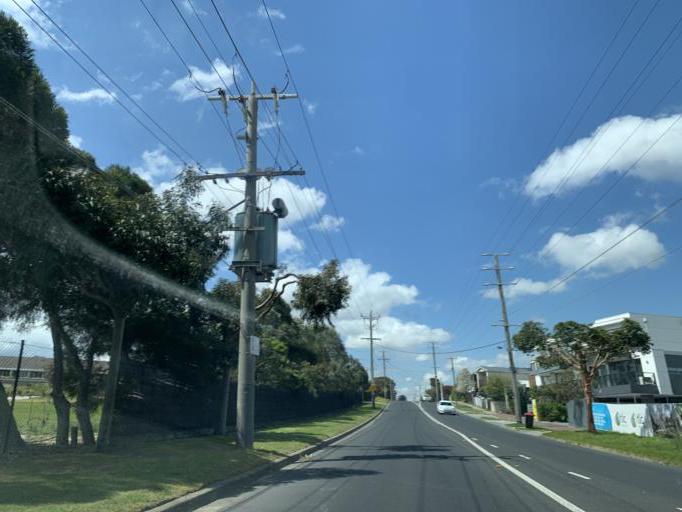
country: AU
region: Victoria
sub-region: Kingston
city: Mordialloc
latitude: -37.9998
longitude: 145.0963
